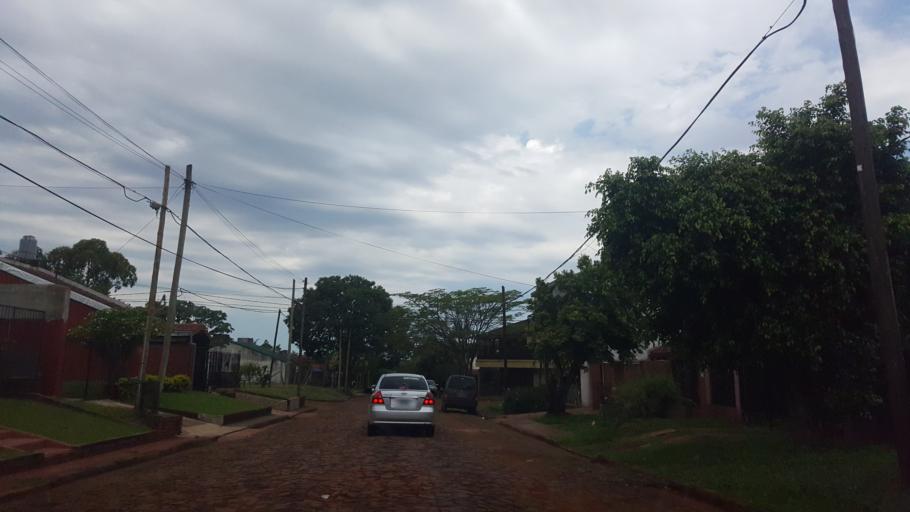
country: AR
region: Misiones
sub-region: Departamento de Capital
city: Posadas
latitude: -27.3981
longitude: -55.9129
